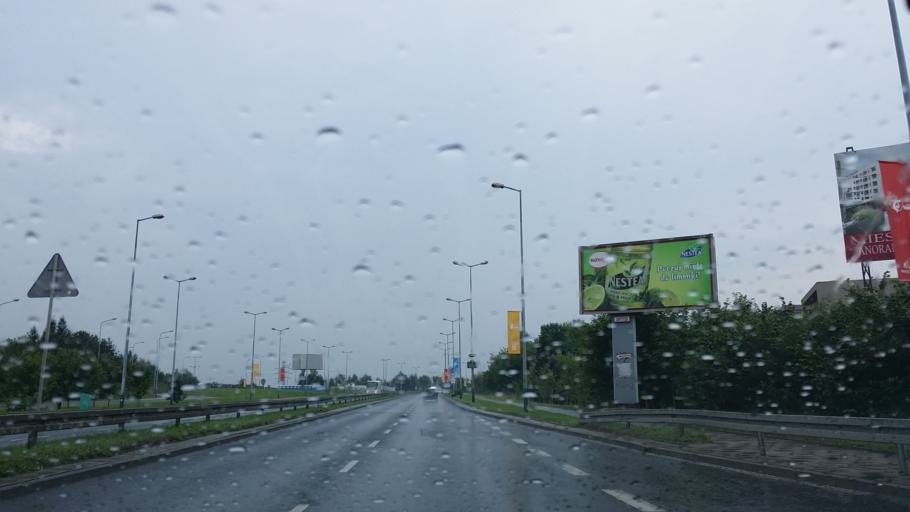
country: PL
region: Lesser Poland Voivodeship
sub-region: Krakow
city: Krakow
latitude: 50.0254
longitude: 19.9452
